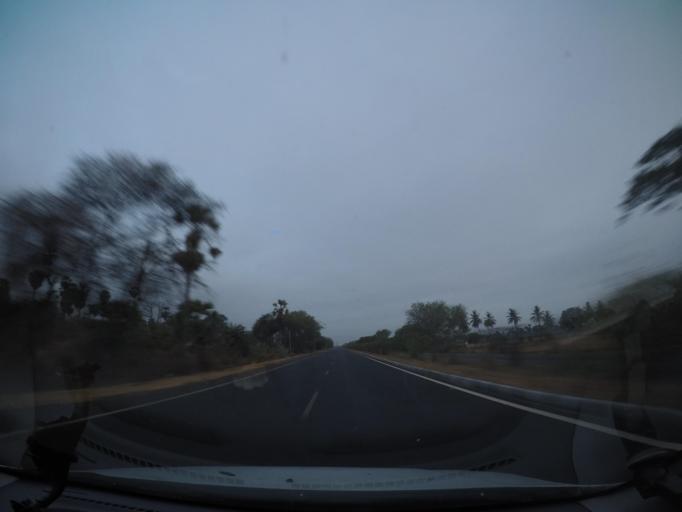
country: IN
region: Andhra Pradesh
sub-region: West Godavari
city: Tadepallegudem
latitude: 16.8101
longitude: 81.3429
